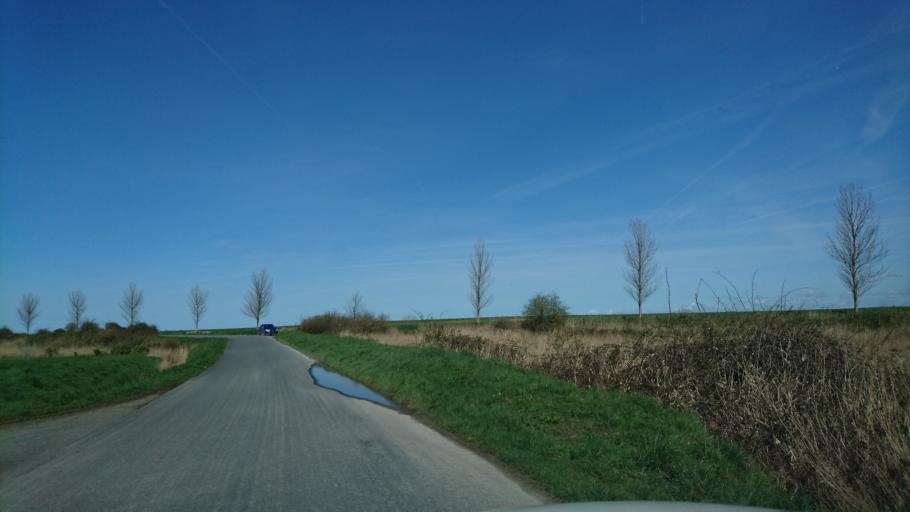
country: FR
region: Brittany
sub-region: Departement d'Ille-et-Vilaine
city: Saint-Broladre
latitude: 48.6089
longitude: -1.6674
